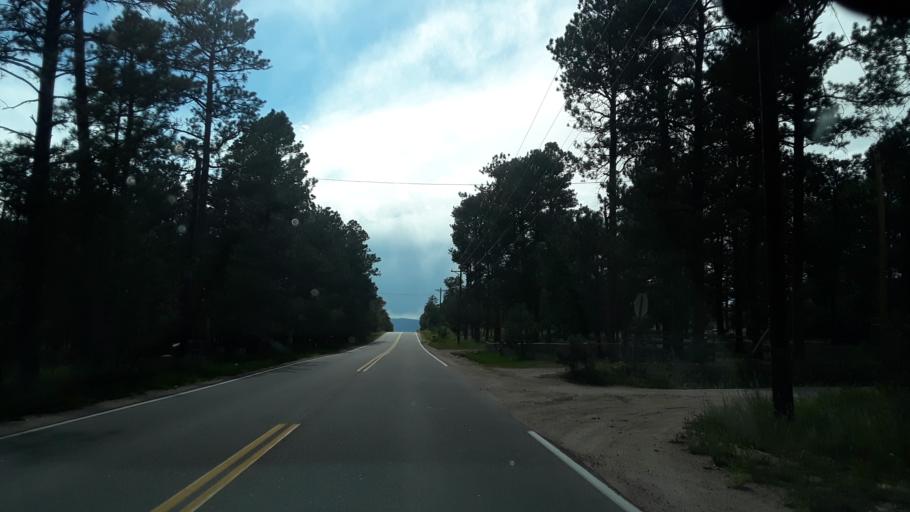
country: US
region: Colorado
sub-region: El Paso County
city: Black Forest
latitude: 39.0128
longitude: -104.7320
